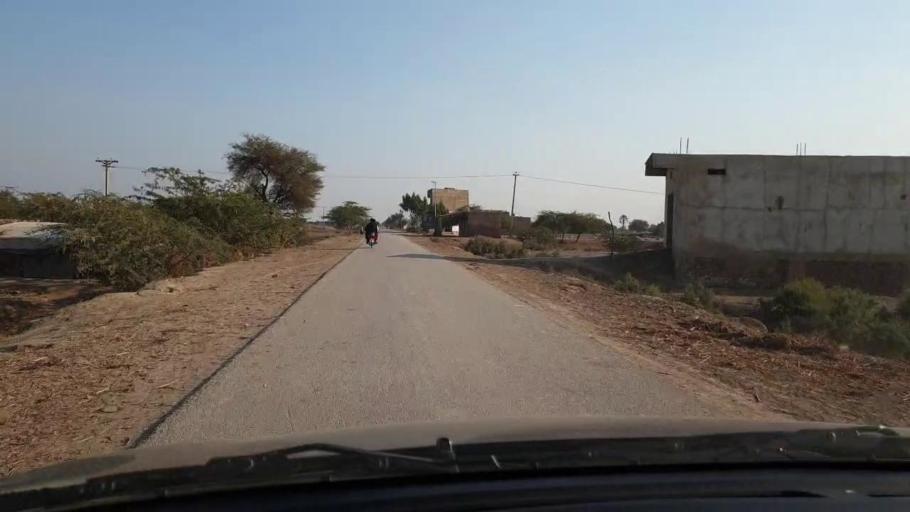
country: PK
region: Sindh
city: Jhol
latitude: 25.9586
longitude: 68.8955
